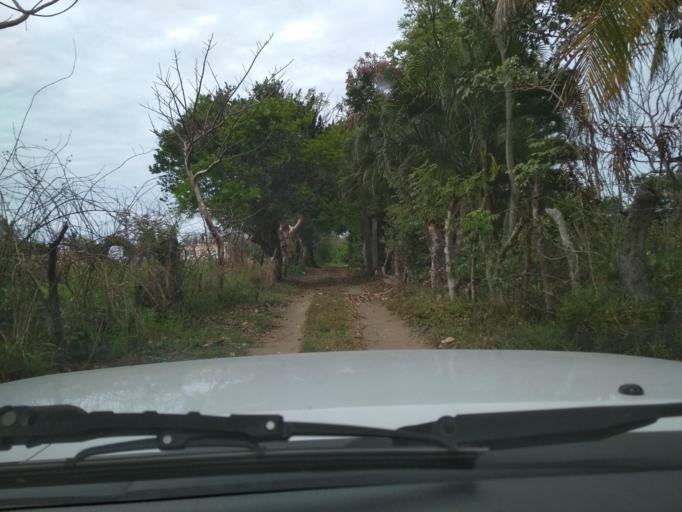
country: MX
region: Veracruz
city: Anton Lizardo
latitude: 19.0532
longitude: -95.9858
